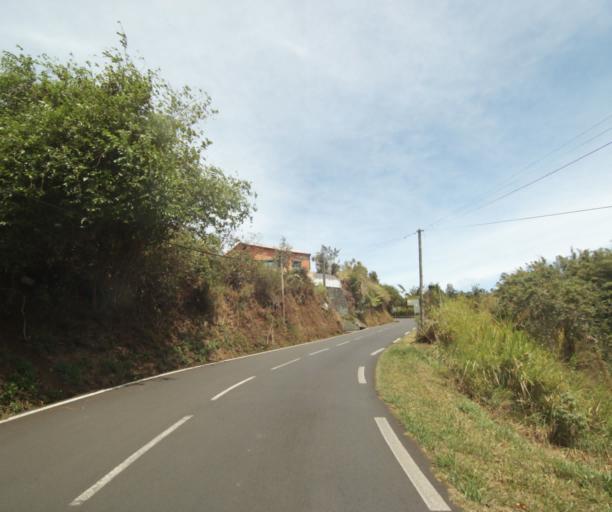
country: RE
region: Reunion
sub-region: Reunion
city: Saint-Paul
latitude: -21.0438
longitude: 55.3076
